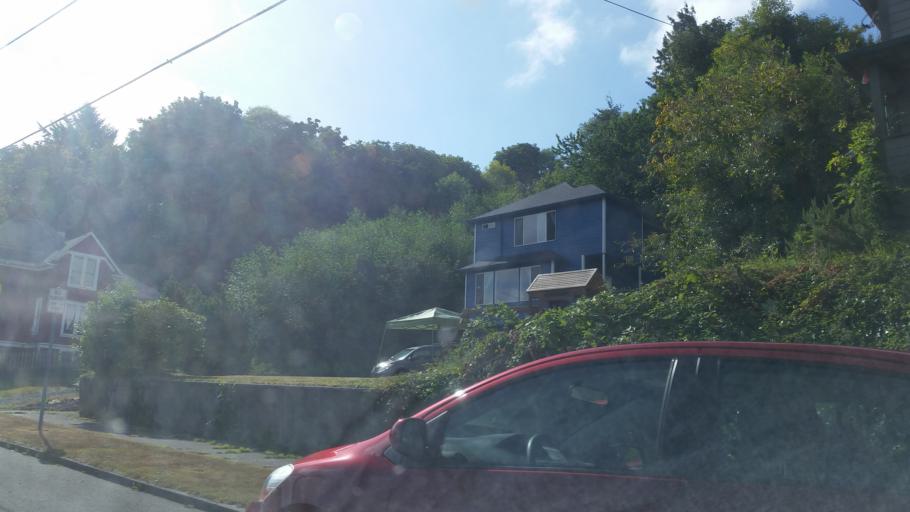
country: US
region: Oregon
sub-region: Clatsop County
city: Astoria
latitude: 46.1914
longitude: -123.8049
